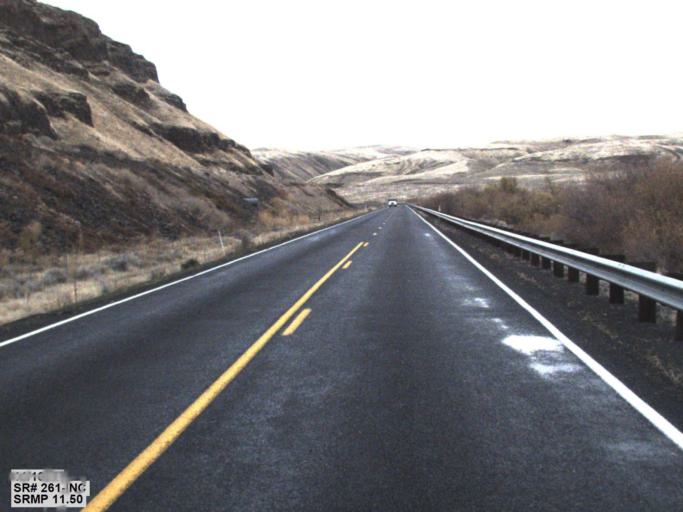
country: US
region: Washington
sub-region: Walla Walla County
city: Waitsburg
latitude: 46.5515
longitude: -118.1793
